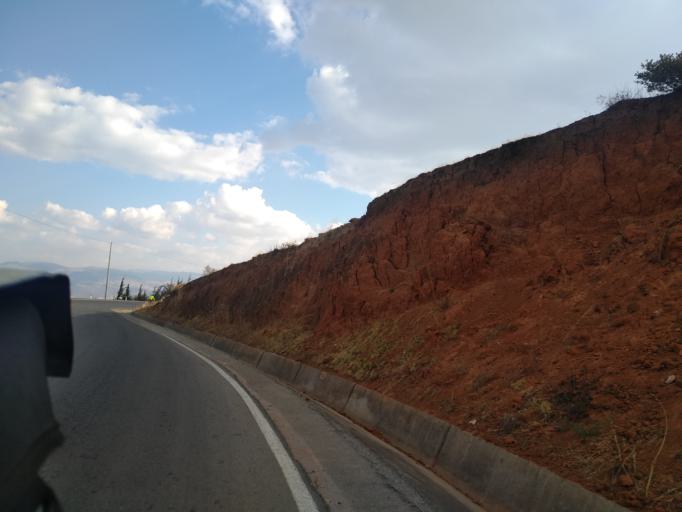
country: PE
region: Cajamarca
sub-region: Provincia de Cajamarca
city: Llacanora
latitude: -7.1531
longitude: -78.4144
